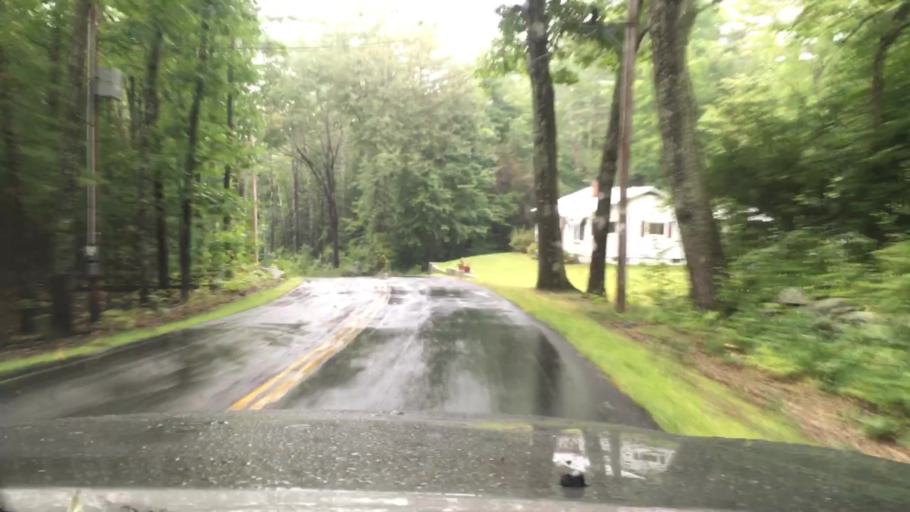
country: US
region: New Hampshire
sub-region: Belknap County
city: Meredith
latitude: 43.6719
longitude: -71.5307
